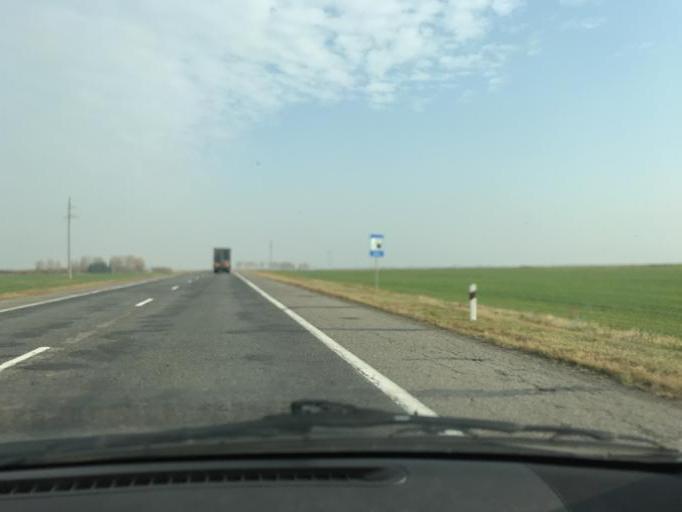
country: BY
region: Vitebsk
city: Chashniki
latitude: 55.0118
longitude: 29.1643
